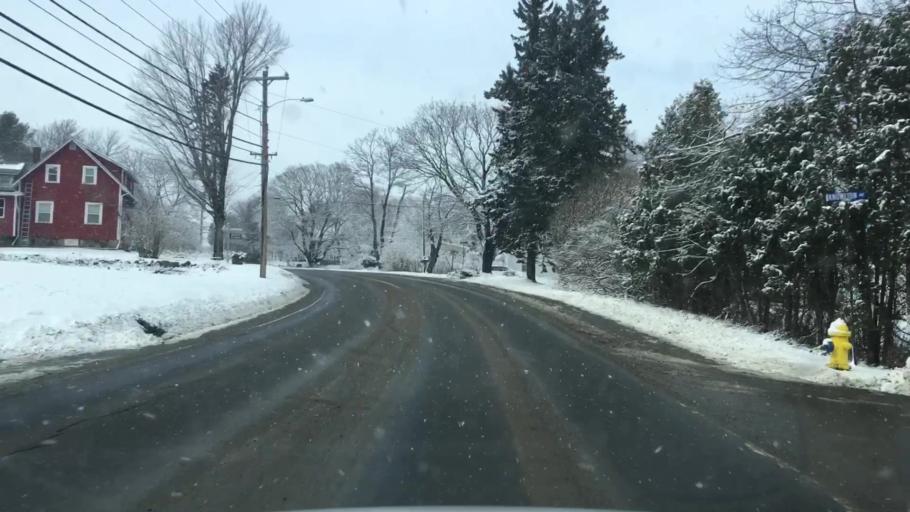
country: US
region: Maine
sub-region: Knox County
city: Rockland
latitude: 44.0852
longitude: -69.1062
